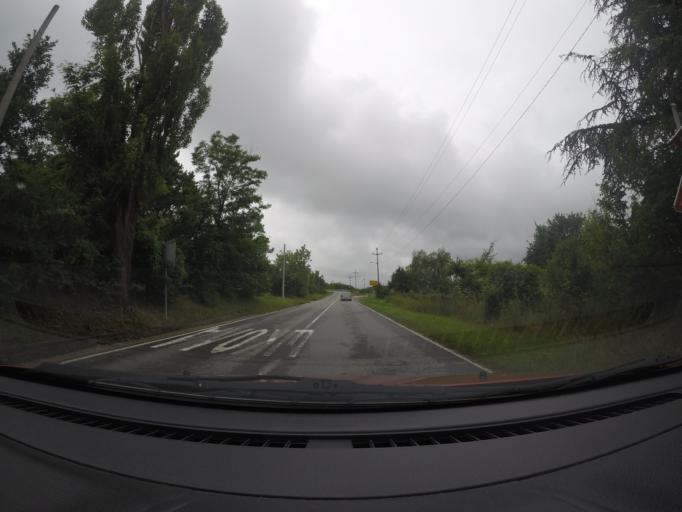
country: RS
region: Central Serbia
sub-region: Belgrade
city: Sopot
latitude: 44.6296
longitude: 20.5544
